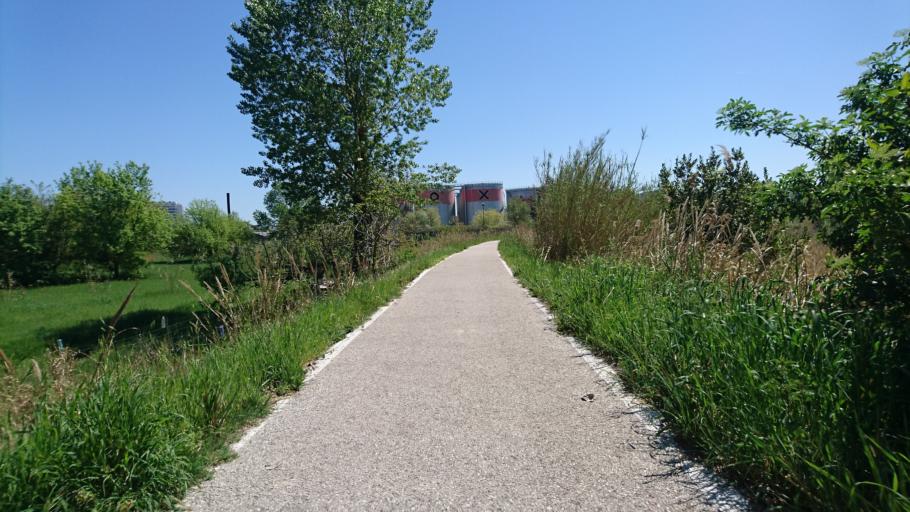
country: IT
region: The Marches
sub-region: Provincia di Pesaro e Urbino
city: Pesaro
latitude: 43.9064
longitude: 12.8820
